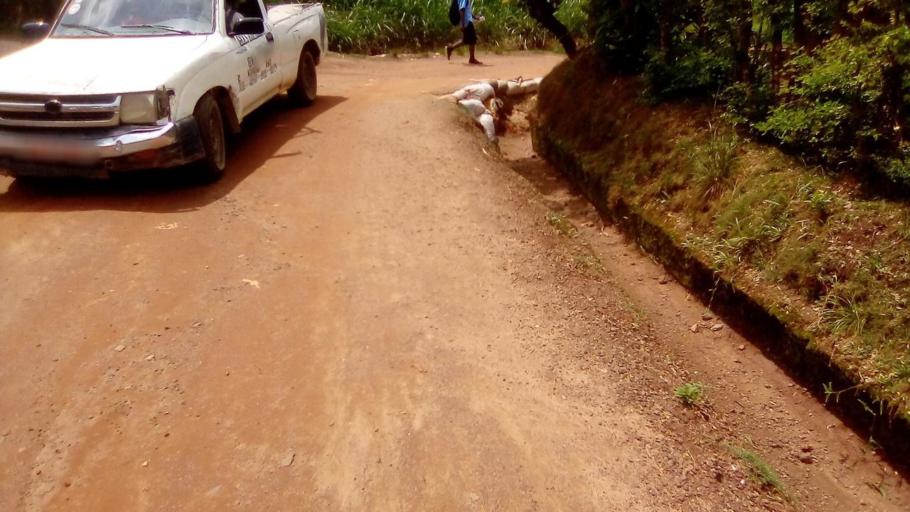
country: SL
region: Southern Province
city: Bo
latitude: 7.9414
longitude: -11.7333
